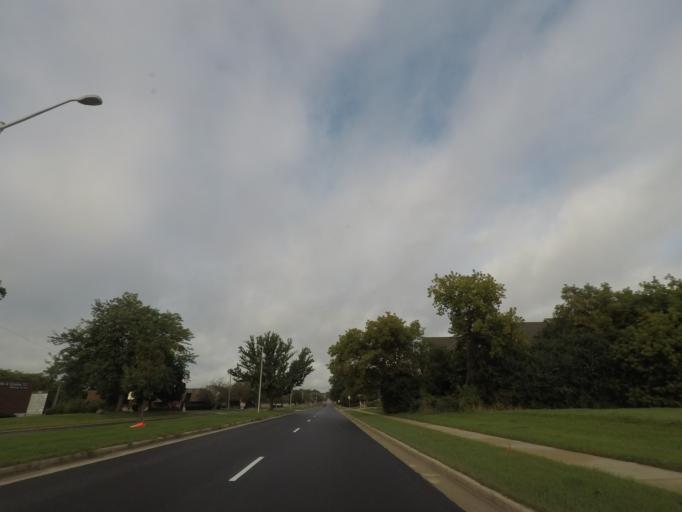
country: US
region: Wisconsin
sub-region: Waukesha County
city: Waukesha
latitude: 43.0250
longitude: -88.2353
